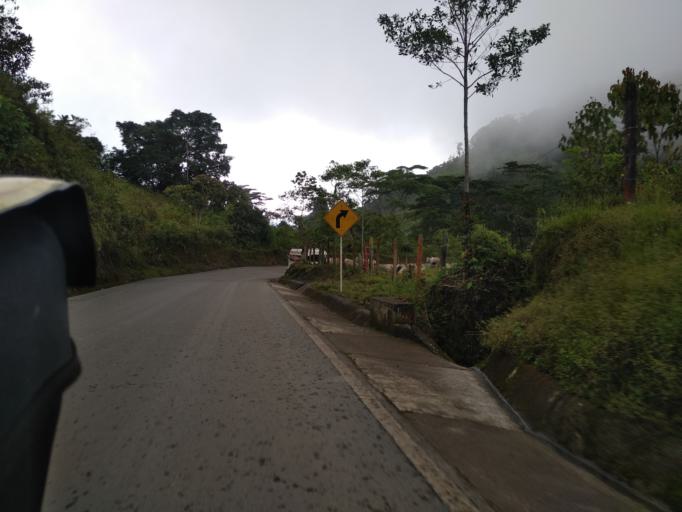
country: CO
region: Santander
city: Landazuri
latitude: 6.1862
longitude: -73.7196
